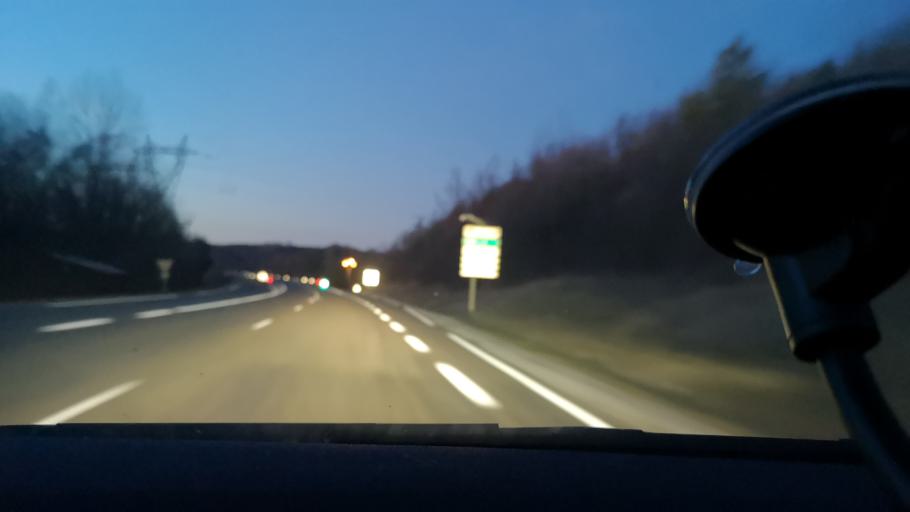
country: FR
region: Franche-Comte
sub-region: Departement du Jura
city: Champagnole
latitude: 46.7579
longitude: 5.9098
